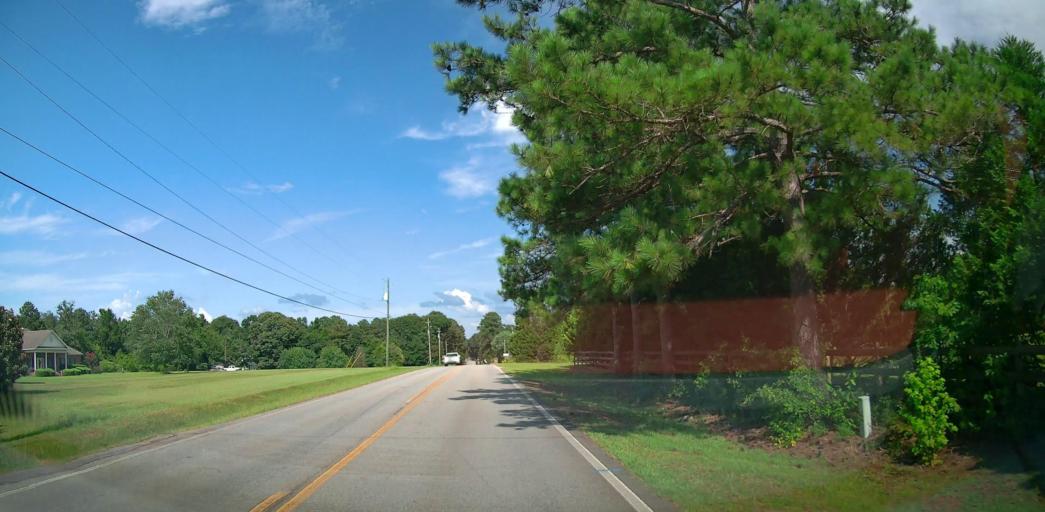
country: US
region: Georgia
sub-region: Houston County
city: Robins Air Force Base
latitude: 32.5380
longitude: -83.6480
